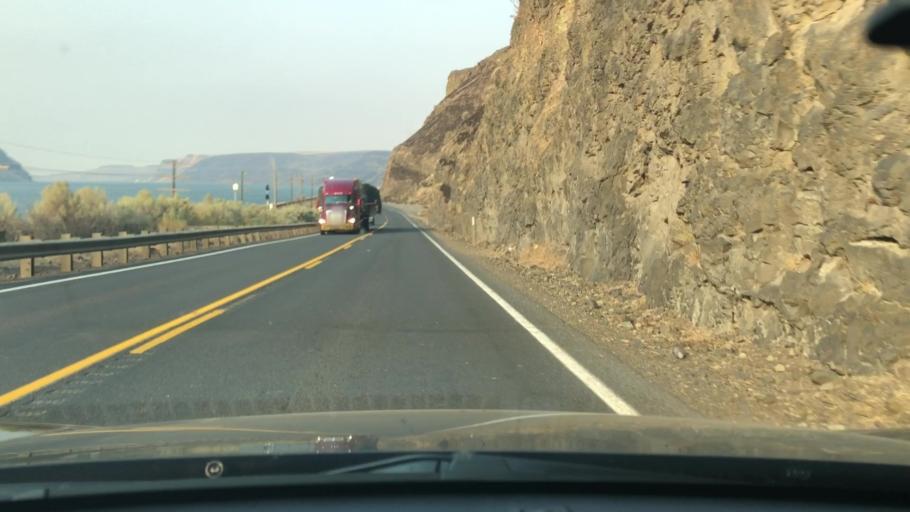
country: US
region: Washington
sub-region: Benton County
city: Highland
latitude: 45.9517
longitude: -119.0561
